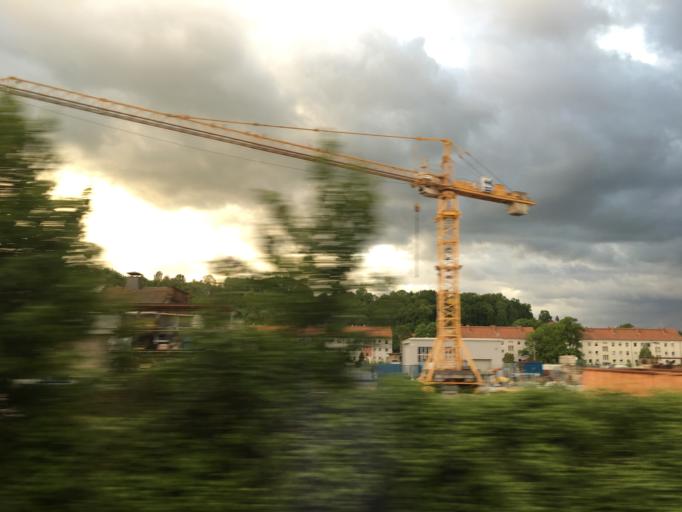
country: DE
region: Saxony
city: Heidenau
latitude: 50.9674
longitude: 13.8816
